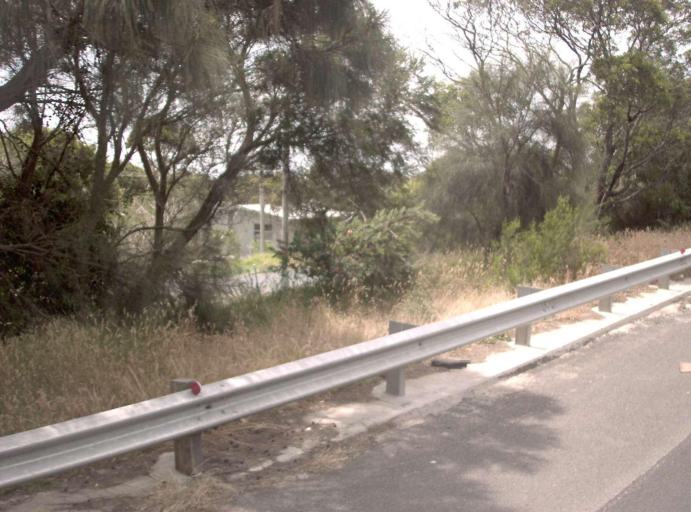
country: AU
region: Victoria
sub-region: Mornington Peninsula
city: McCrae
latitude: -38.3516
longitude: 144.9335
